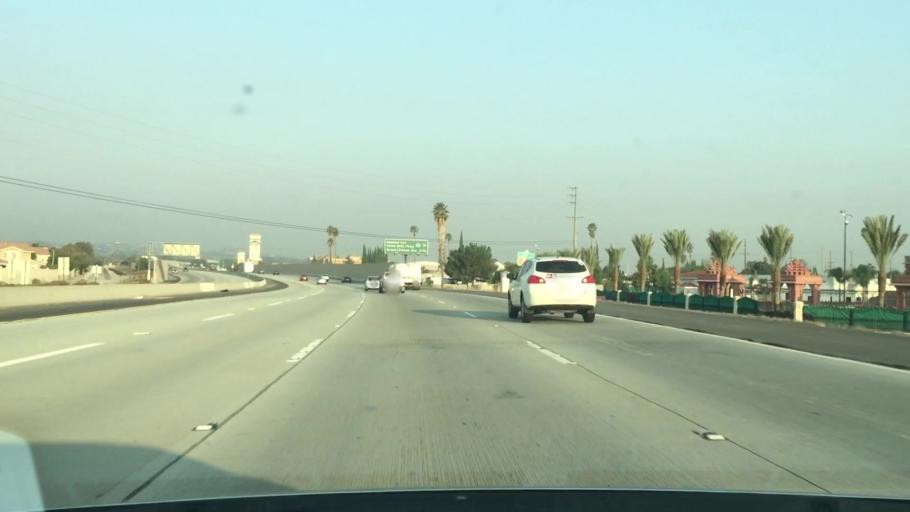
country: US
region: California
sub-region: San Bernardino County
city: Los Serranos
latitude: 33.9750
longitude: -117.6964
